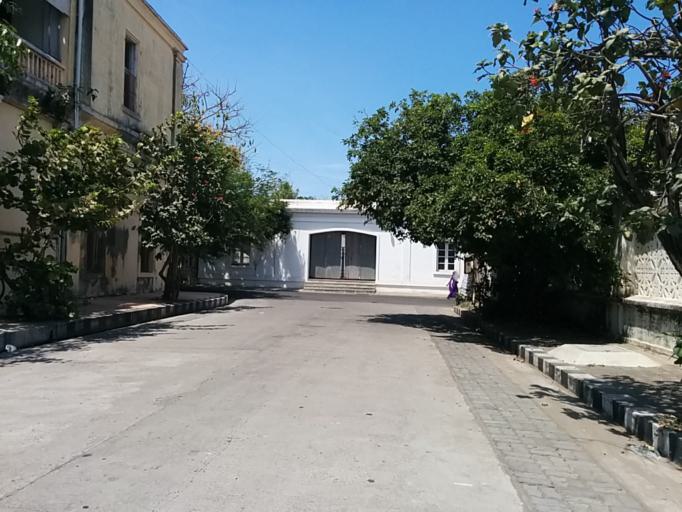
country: IN
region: Pondicherry
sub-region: Puducherry
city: Puducherry
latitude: 11.9314
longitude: 79.8350
